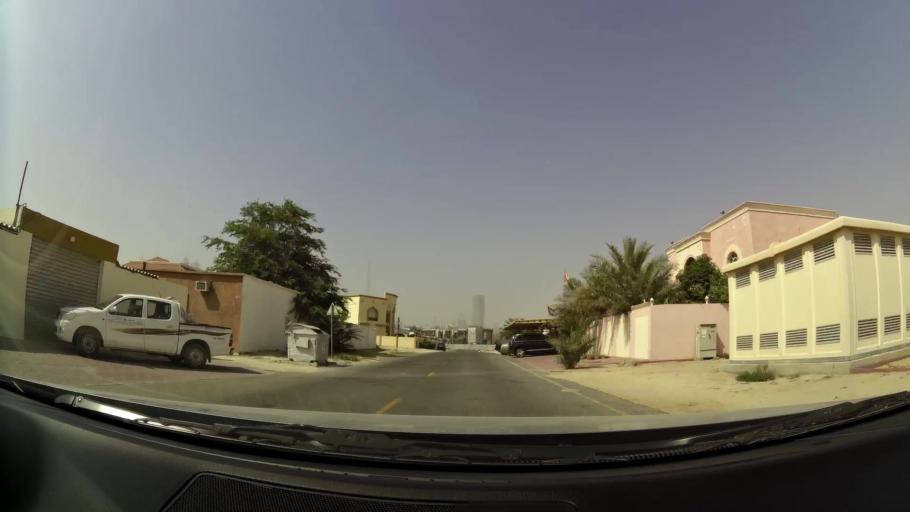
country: AE
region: Dubai
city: Dubai
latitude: 25.1657
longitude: 55.2568
